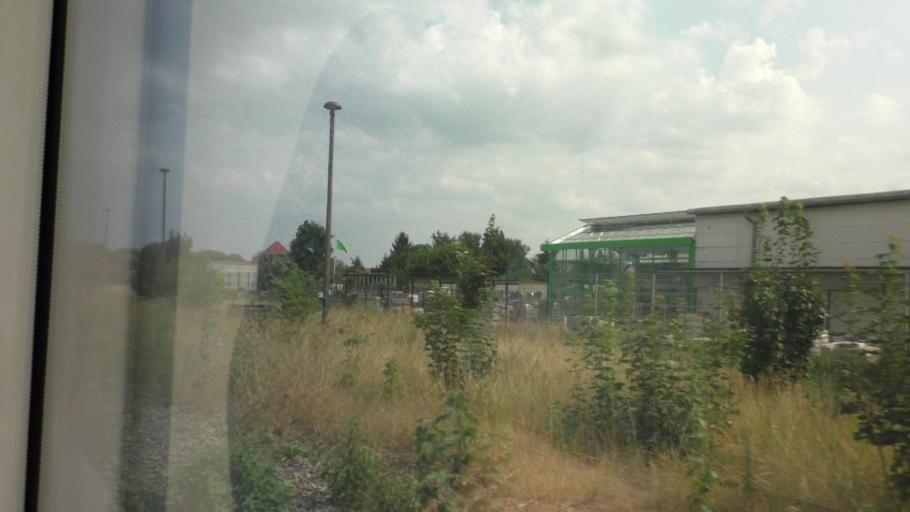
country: DE
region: Brandenburg
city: Beeskow
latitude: 52.1773
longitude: 14.2435
